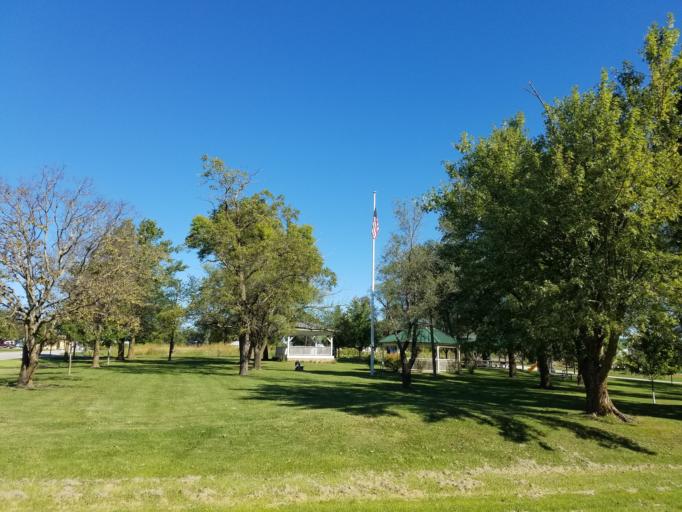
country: US
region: Iowa
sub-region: Decatur County
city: Leon
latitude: 40.5802
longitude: -93.7441
